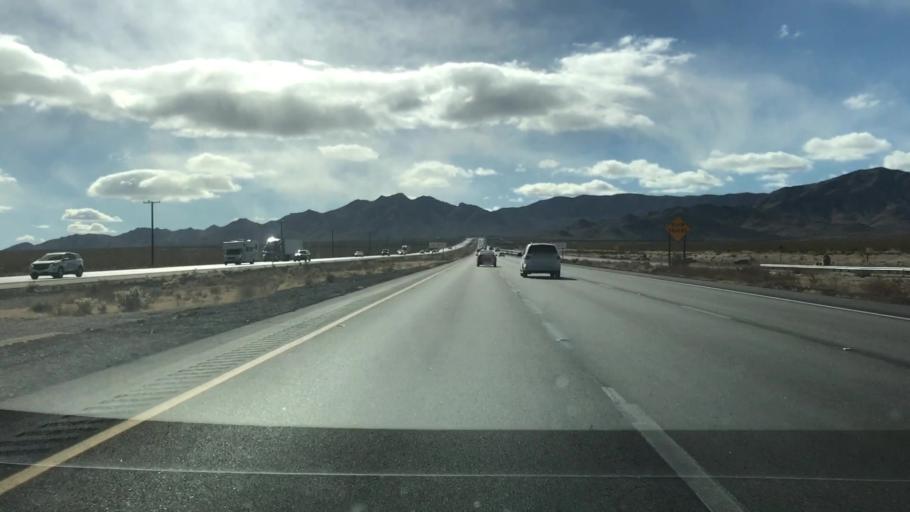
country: US
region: Nevada
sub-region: Clark County
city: Sandy Valley
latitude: 35.5016
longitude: -115.4367
